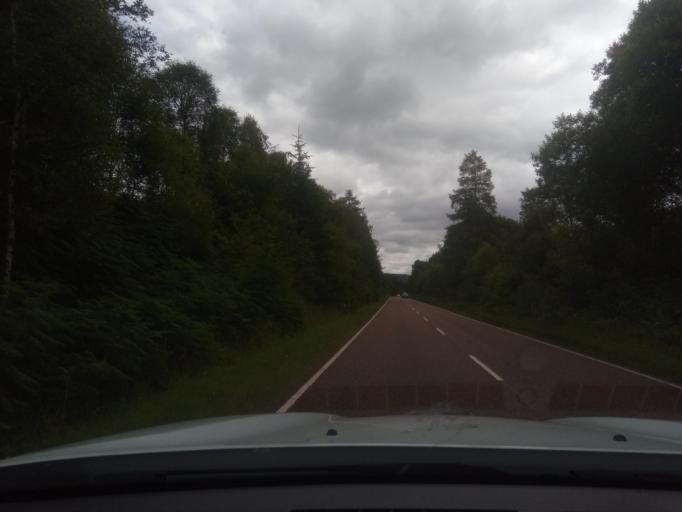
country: GB
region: Scotland
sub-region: Highland
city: Fort William
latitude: 56.8557
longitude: -5.2115
